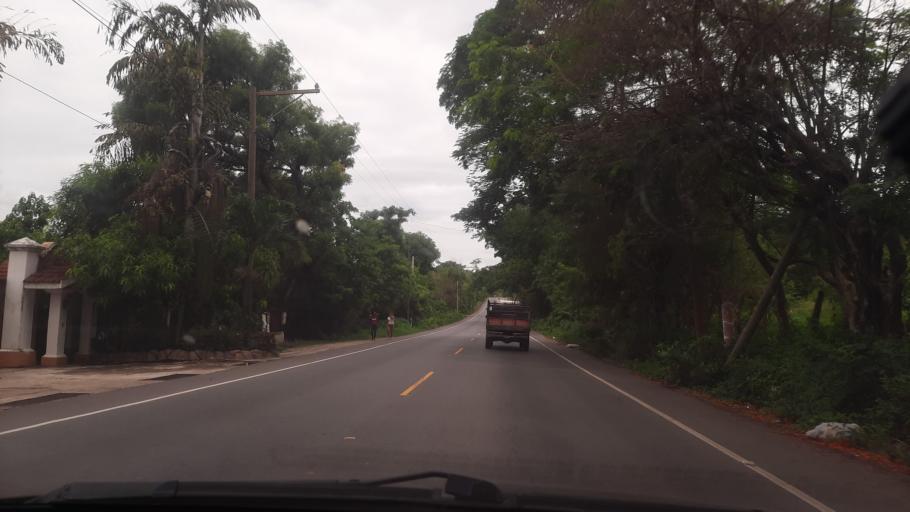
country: GT
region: Zacapa
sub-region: Municipio de Zacapa
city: Gualan
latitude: 15.1418
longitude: -89.3328
